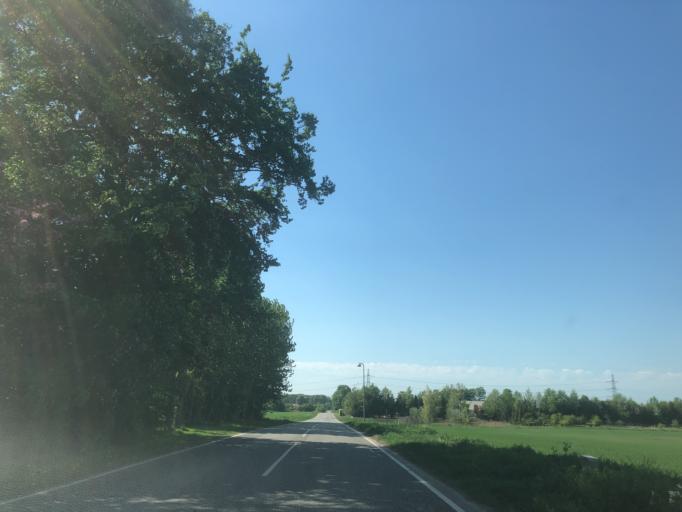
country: DK
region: Capital Region
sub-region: Hoje-Taastrup Kommune
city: Taastrup
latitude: 55.6278
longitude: 12.2369
